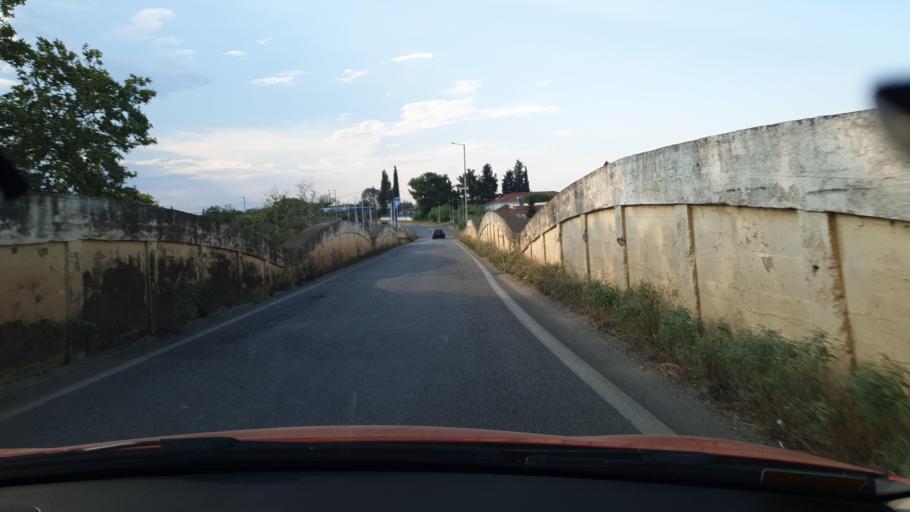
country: GR
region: Thessaly
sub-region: Nomos Magnisias
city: Almyros
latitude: 39.1596
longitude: 22.7986
